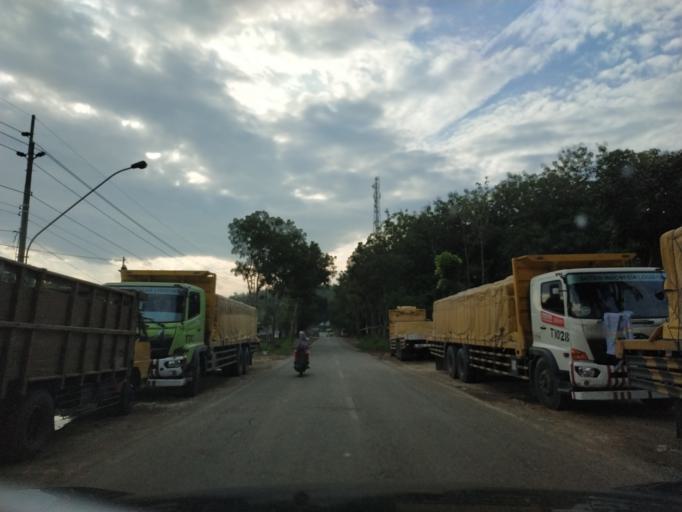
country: ID
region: Central Java
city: Ngampel
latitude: -6.9014
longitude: 111.4417
